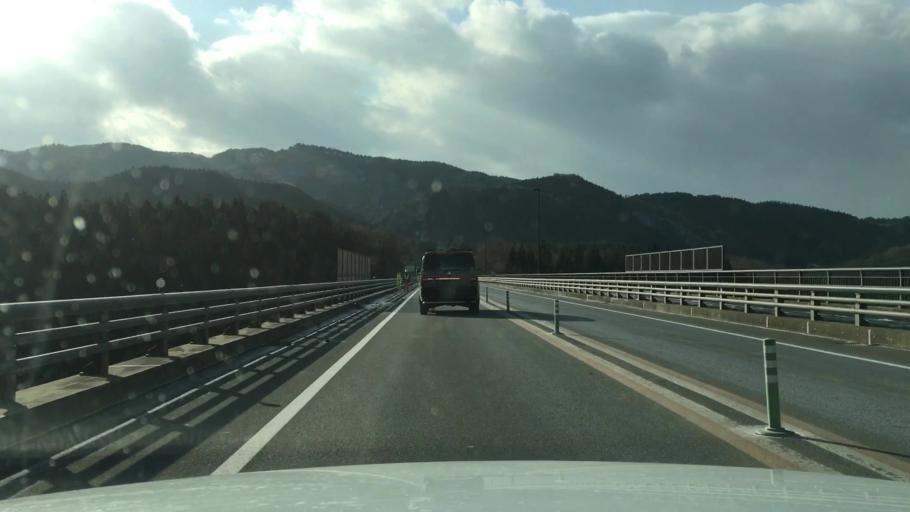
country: JP
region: Iwate
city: Morioka-shi
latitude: 39.6681
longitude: 141.2501
